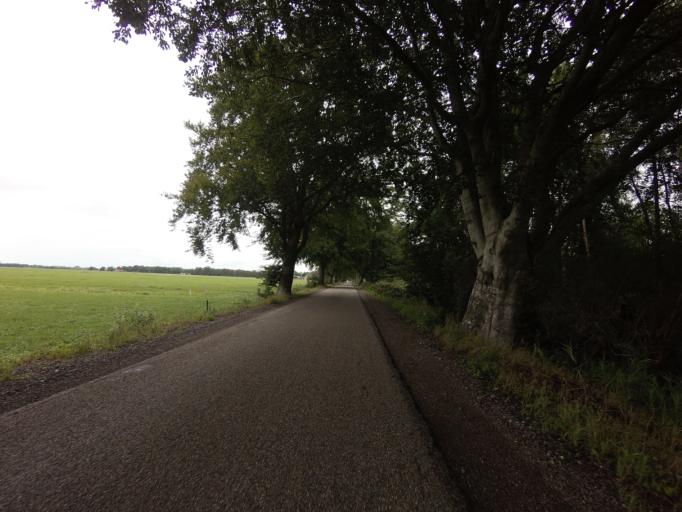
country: NL
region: Friesland
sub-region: Gemeente Weststellingwerf
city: Steggerda
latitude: 52.8767
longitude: 6.0925
